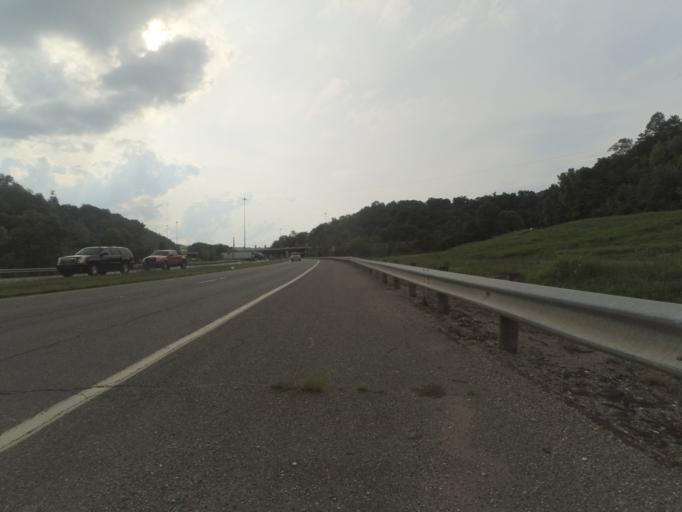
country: US
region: West Virginia
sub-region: Cabell County
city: Huntington
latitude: 38.3925
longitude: -82.4021
